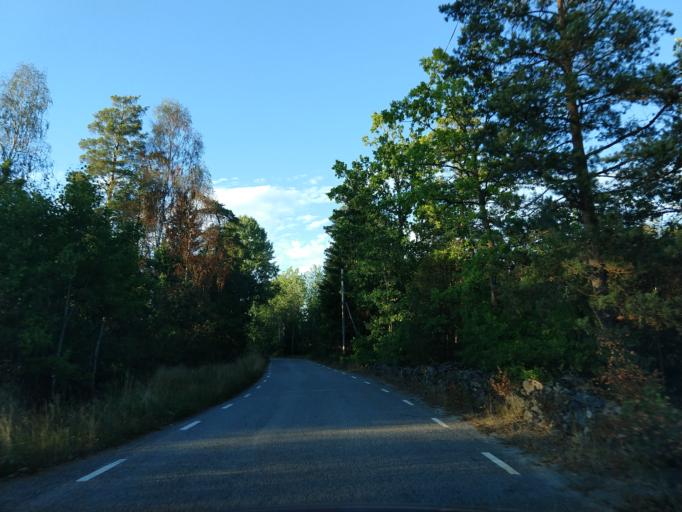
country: SE
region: Blekinge
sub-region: Ronneby Kommun
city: Brakne-Hoby
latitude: 56.2760
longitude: 15.1632
